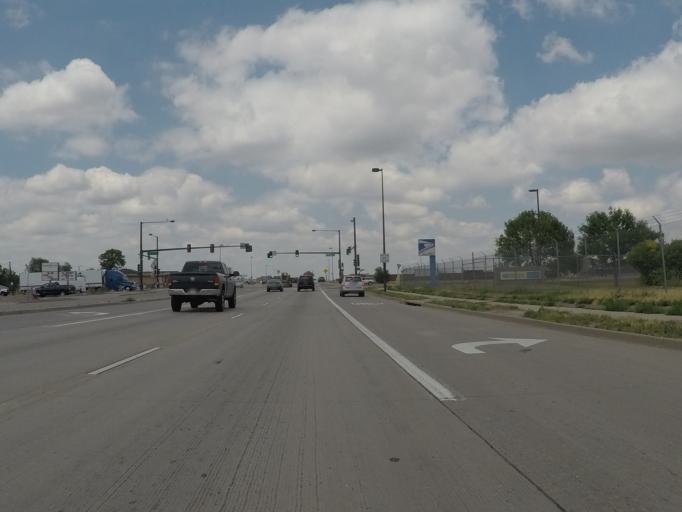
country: US
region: Colorado
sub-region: Adams County
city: Commerce City
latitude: 39.7927
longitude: -104.9033
